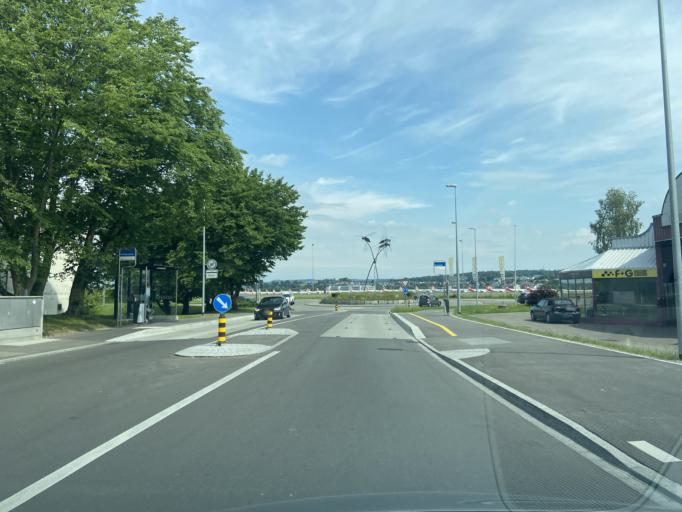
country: CH
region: Zurich
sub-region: Bezirk Uster
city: Duebendorf / Sonnenberg
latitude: 47.3947
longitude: 8.6403
